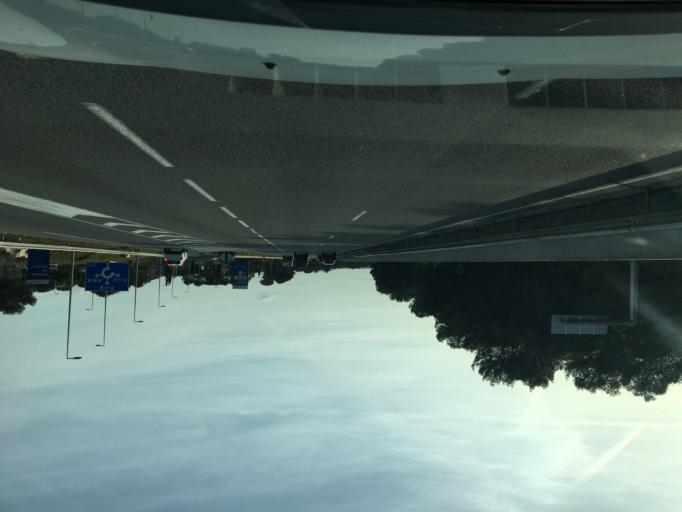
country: FR
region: Provence-Alpes-Cote d'Azur
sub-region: Departement du Var
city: Puget-sur-Argens
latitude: 43.4655
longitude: 6.6743
